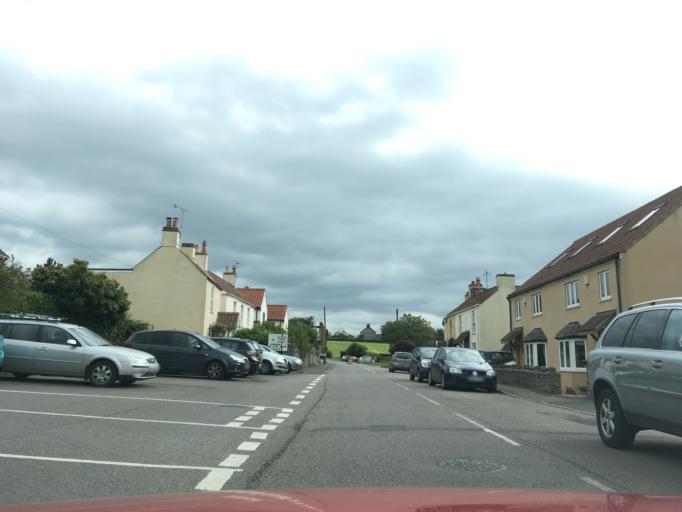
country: GB
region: England
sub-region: South Gloucestershire
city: Almondsbury
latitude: 51.5801
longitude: -2.5769
